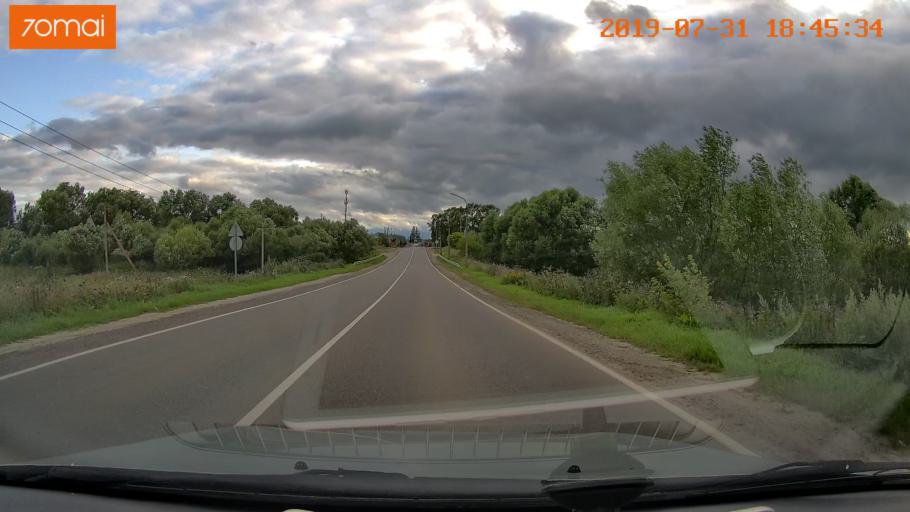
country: RU
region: Moskovskaya
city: Troitskoye
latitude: 55.2507
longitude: 38.5307
